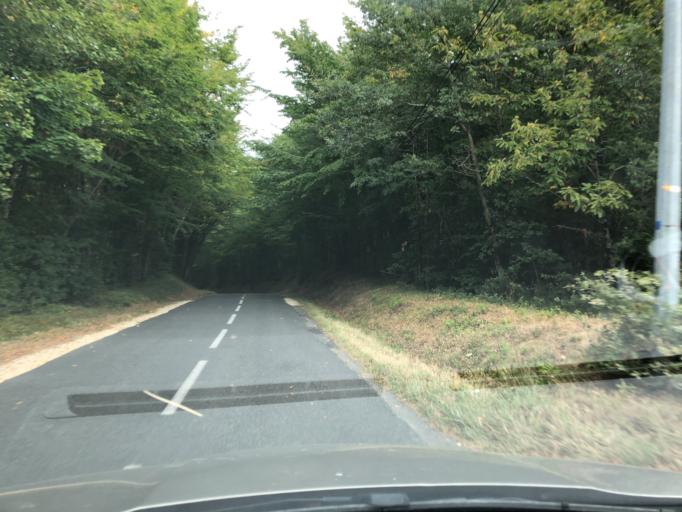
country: FR
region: Centre
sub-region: Departement d'Indre-et-Loire
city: Mazieres-de-Touraine
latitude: 47.3897
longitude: 0.4501
